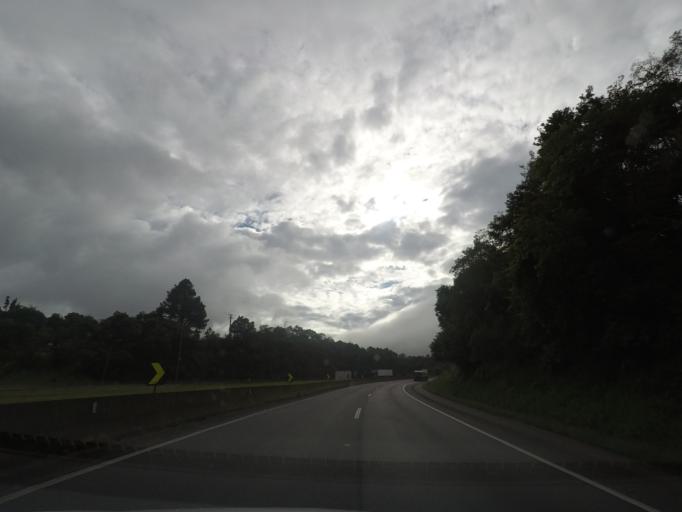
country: BR
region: Parana
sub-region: Campina Grande Do Sul
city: Campina Grande do Sul
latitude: -25.1776
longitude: -48.8784
